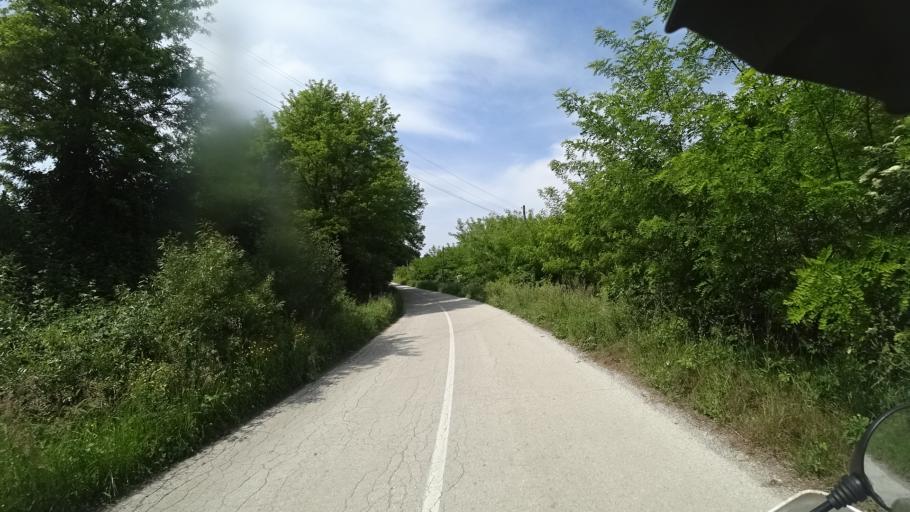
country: HR
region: Sisacko-Moslavacka
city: Gvozd
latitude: 45.3473
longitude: 15.8653
